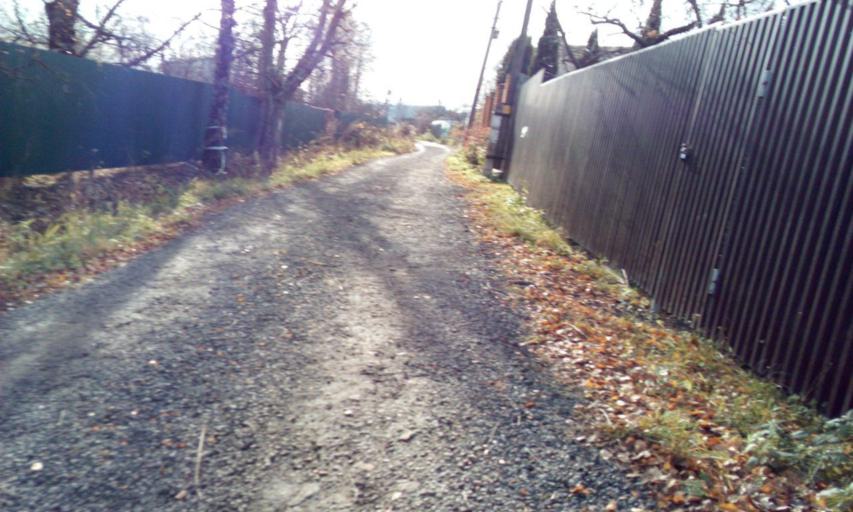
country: RU
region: Moskovskaya
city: Zhavoronki
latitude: 55.6545
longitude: 37.1519
